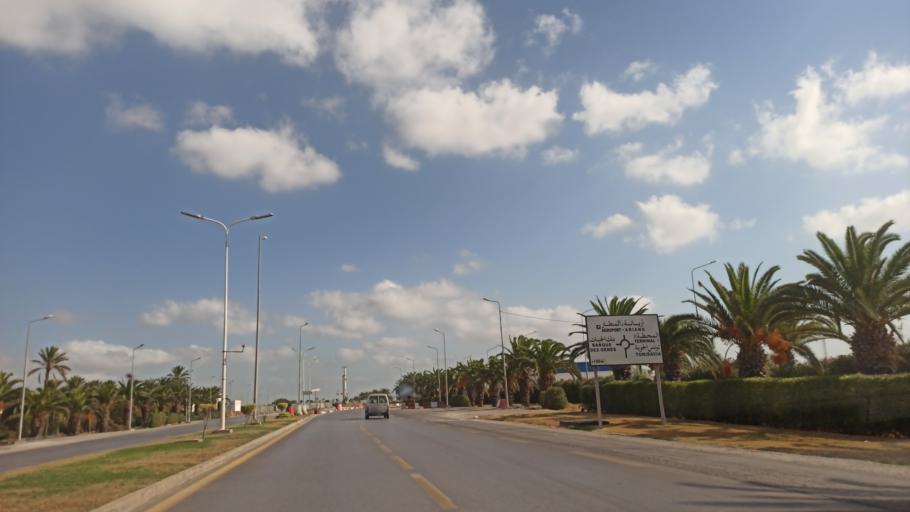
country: TN
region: Ariana
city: Ariana
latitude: 36.8389
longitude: 10.2138
